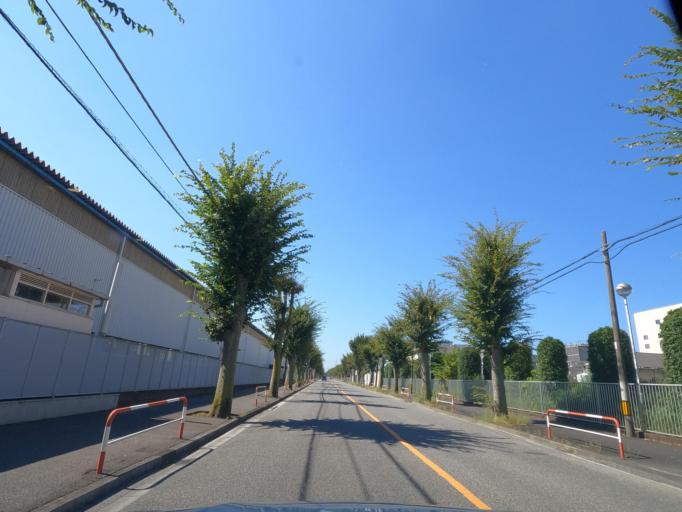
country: JP
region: Saitama
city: Kawagoe
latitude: 35.8870
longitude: 139.4467
